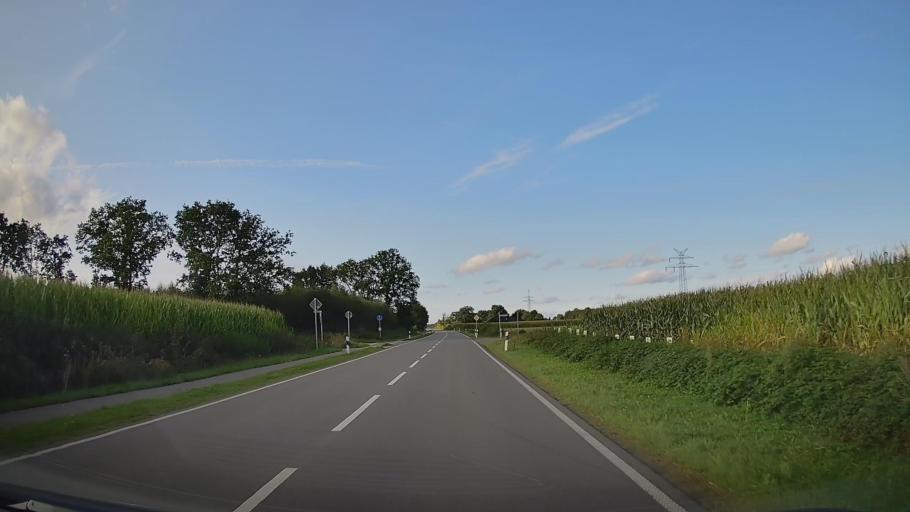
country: DE
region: Lower Saxony
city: Barssel
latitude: 53.1044
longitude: 7.7091
